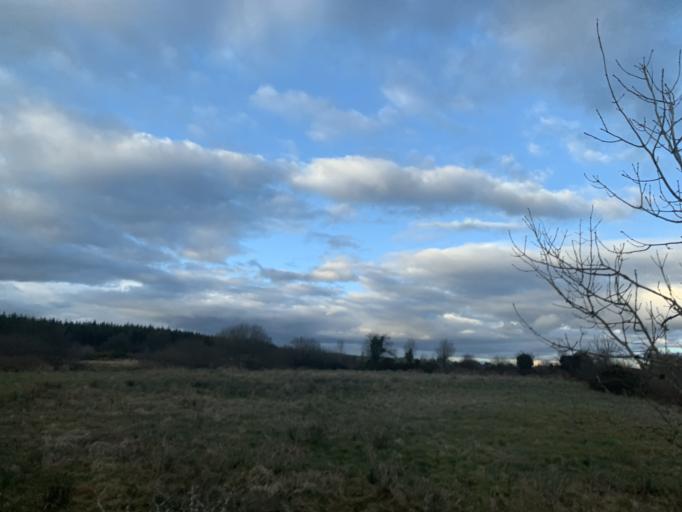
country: IE
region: Connaught
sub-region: Maigh Eo
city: Ballyhaunis
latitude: 53.8647
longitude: -8.7588
